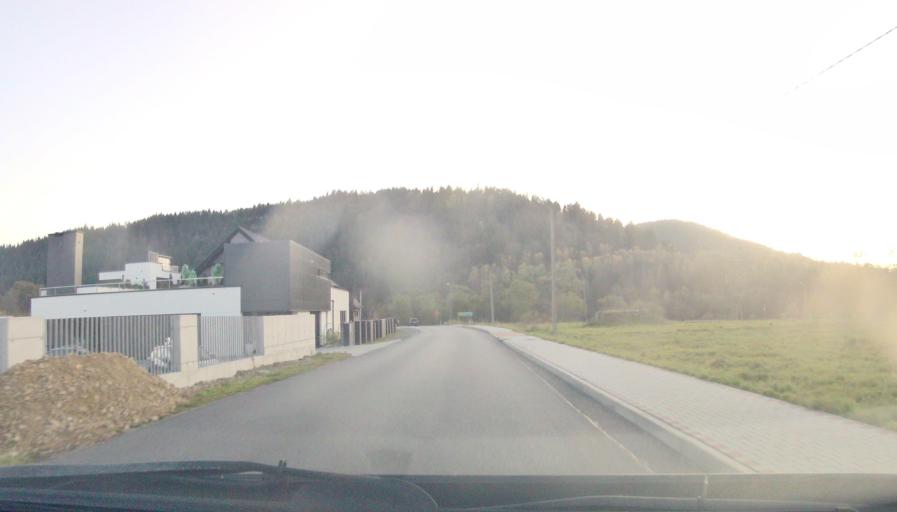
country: PL
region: Lesser Poland Voivodeship
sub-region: Powiat suski
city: Kukow
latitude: 49.7413
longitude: 19.4633
